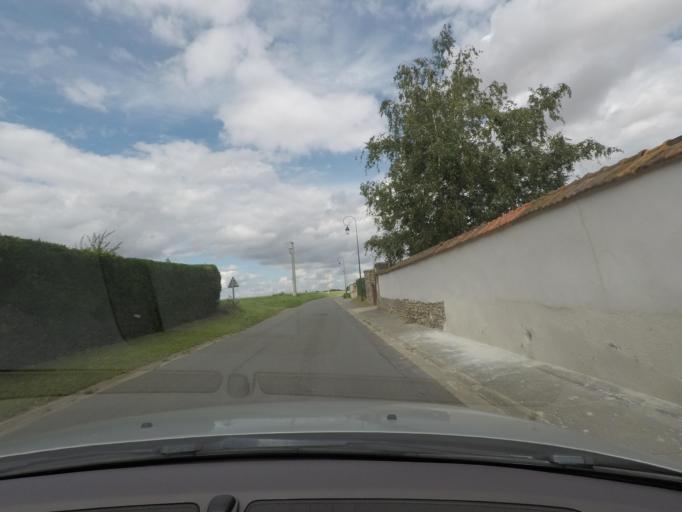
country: FR
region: Haute-Normandie
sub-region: Departement de l'Eure
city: Les Andelys
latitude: 49.1967
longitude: 1.4645
